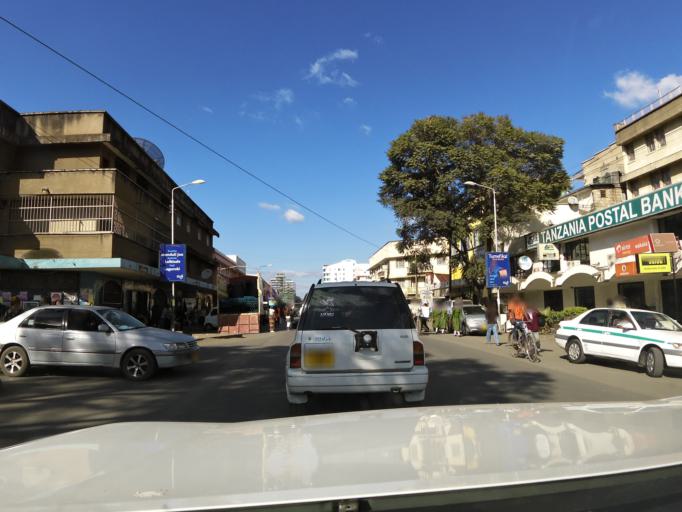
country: TZ
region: Arusha
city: Arusha
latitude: -3.3744
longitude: 36.6832
